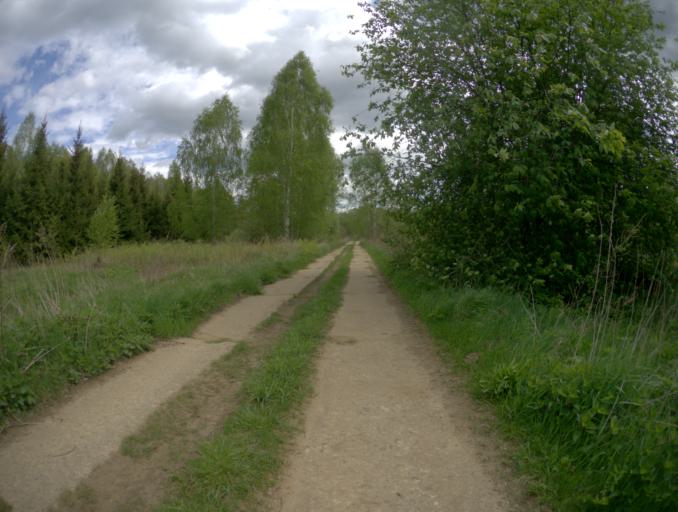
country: RU
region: Moskovskaya
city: Cherusti
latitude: 55.4820
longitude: 40.0329
